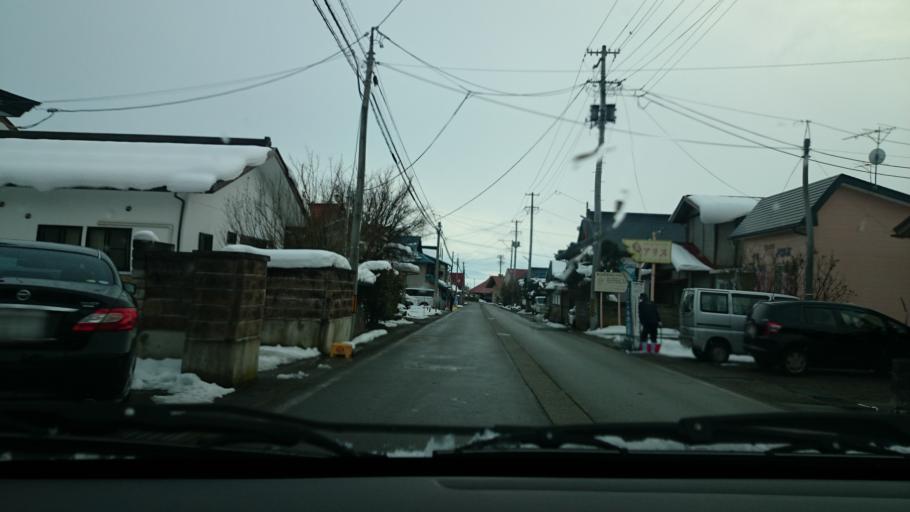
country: JP
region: Fukushima
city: Kitakata
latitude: 37.6337
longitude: 139.9221
